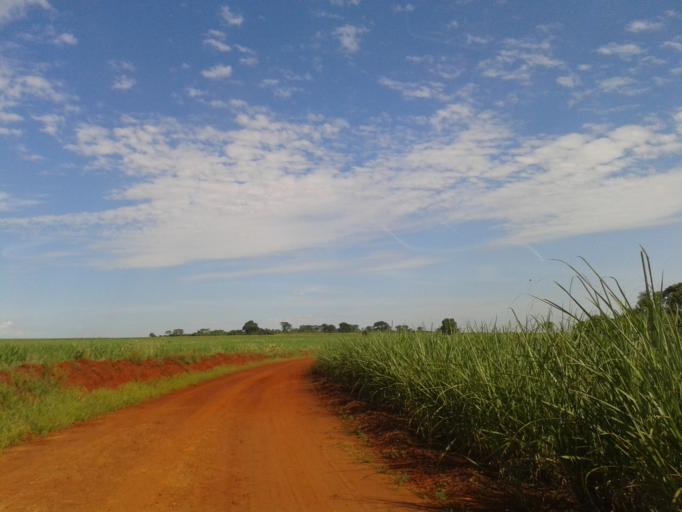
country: BR
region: Minas Gerais
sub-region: Centralina
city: Centralina
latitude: -18.6353
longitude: -49.2587
